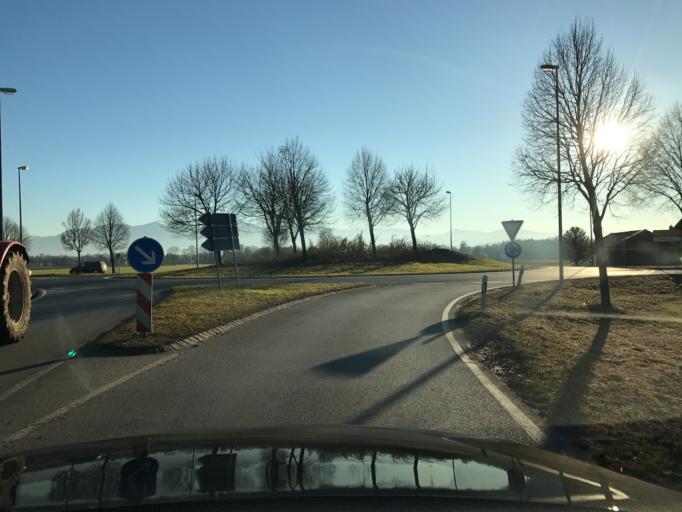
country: DE
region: Bavaria
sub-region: Upper Bavaria
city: Bad Aibling
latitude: 47.8710
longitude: 11.9889
